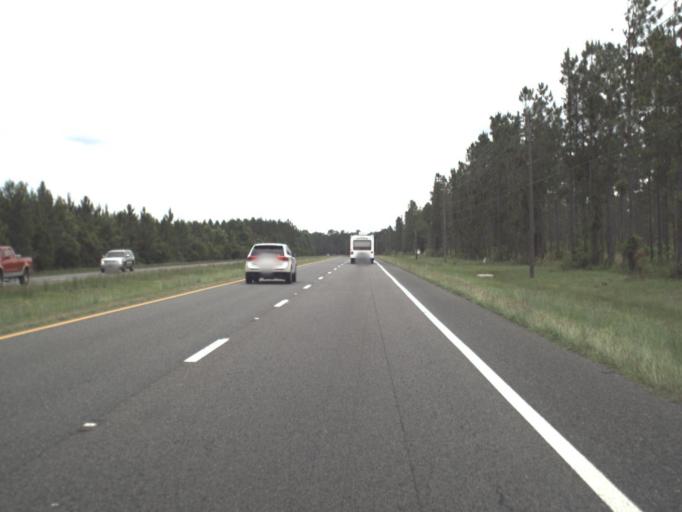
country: US
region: Florida
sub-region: Nassau County
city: Hilliard
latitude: 30.6557
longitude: -81.8777
